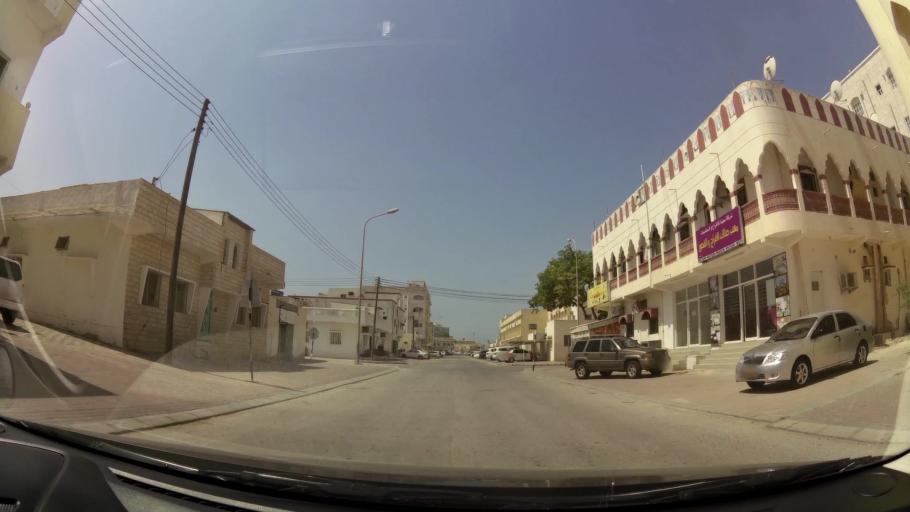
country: OM
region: Zufar
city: Salalah
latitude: 17.0206
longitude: 54.1061
